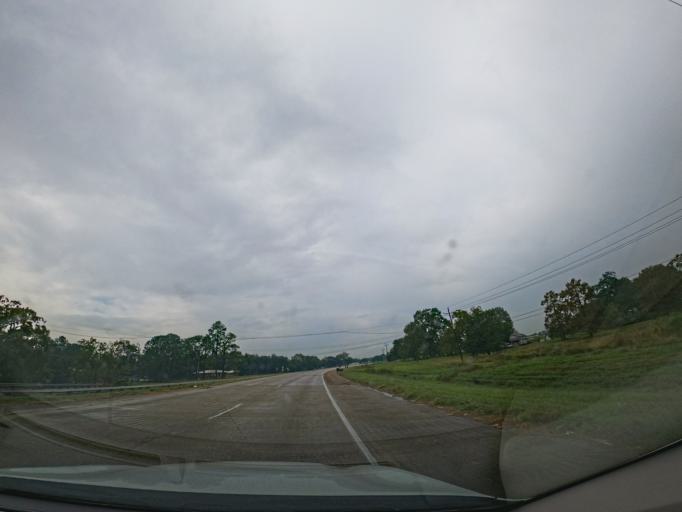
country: US
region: Louisiana
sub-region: Iberia Parish
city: Delcambre
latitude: 29.9679
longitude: -91.9079
